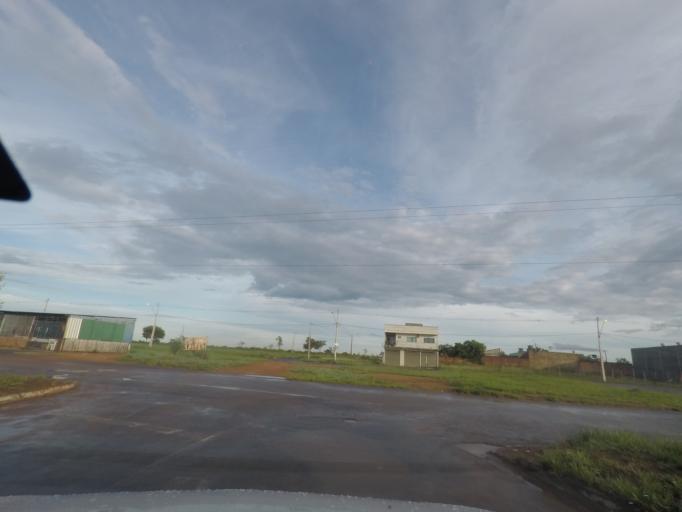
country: BR
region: Goias
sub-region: Trindade
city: Trindade
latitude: -16.7460
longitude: -49.3851
